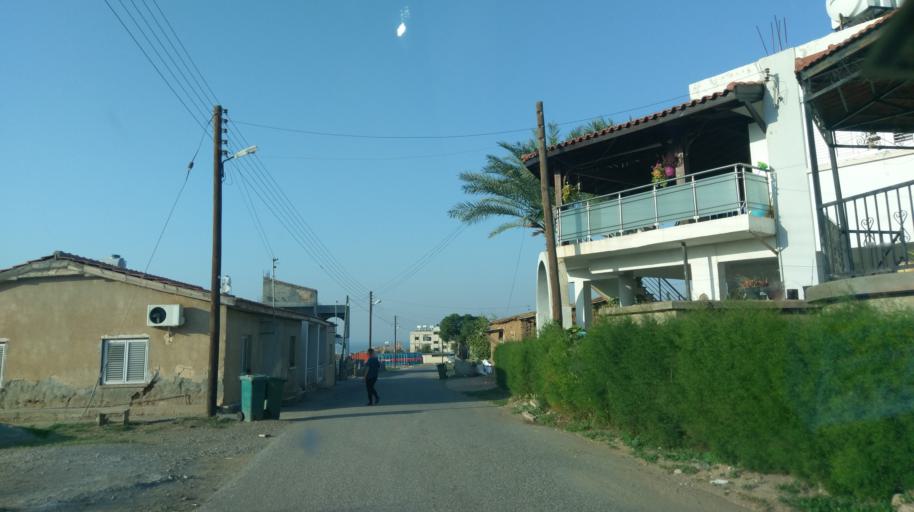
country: CY
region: Lefkosia
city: Lefka
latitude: 35.1292
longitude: 32.9109
